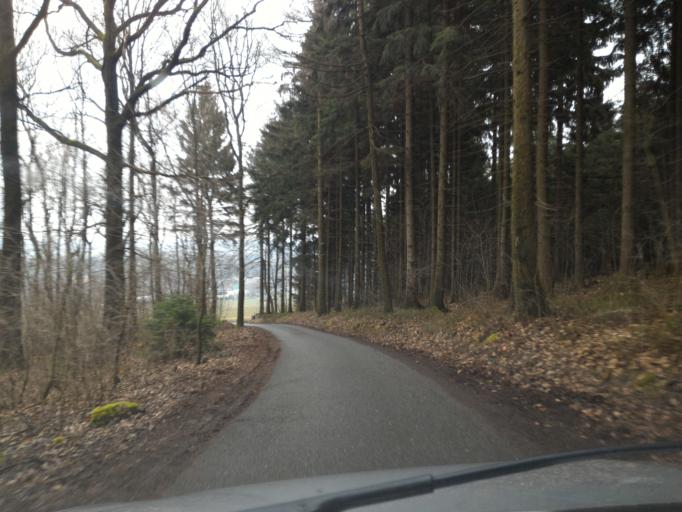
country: DE
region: Saxony
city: Eibau
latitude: 50.9621
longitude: 14.6899
